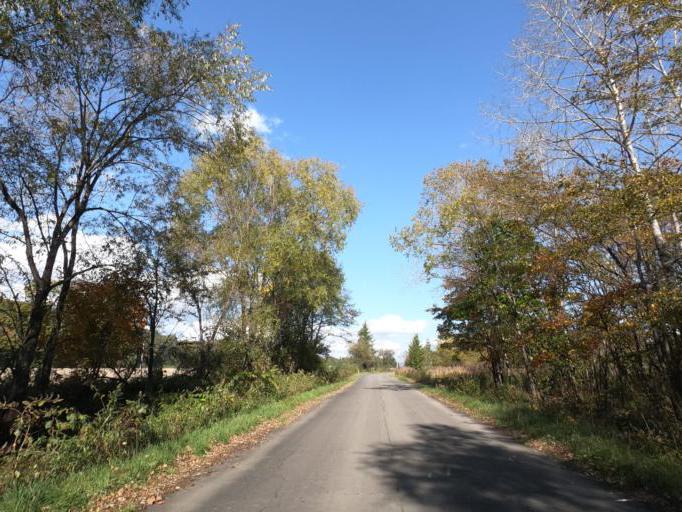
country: JP
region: Hokkaido
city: Otofuke
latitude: 43.2335
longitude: 143.2646
